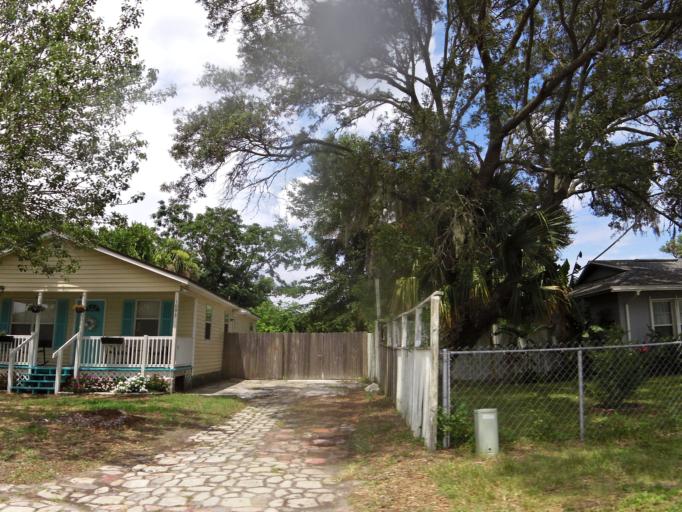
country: US
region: Florida
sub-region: Duval County
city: Atlantic Beach
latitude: 30.3278
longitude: -81.4173
